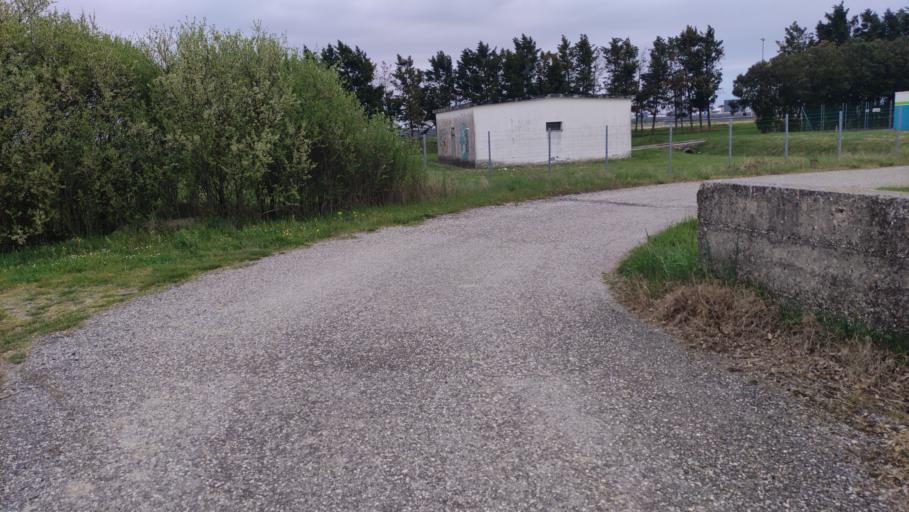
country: IT
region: Emilia-Romagna
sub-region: Provincia di Ravenna
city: Russi
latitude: 44.4021
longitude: 12.0435
